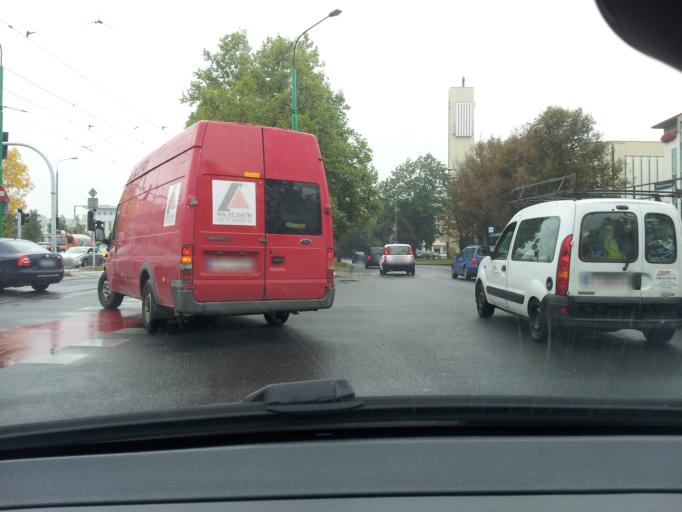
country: PL
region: Greater Poland Voivodeship
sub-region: Poznan
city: Poznan
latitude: 52.4097
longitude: 16.8885
